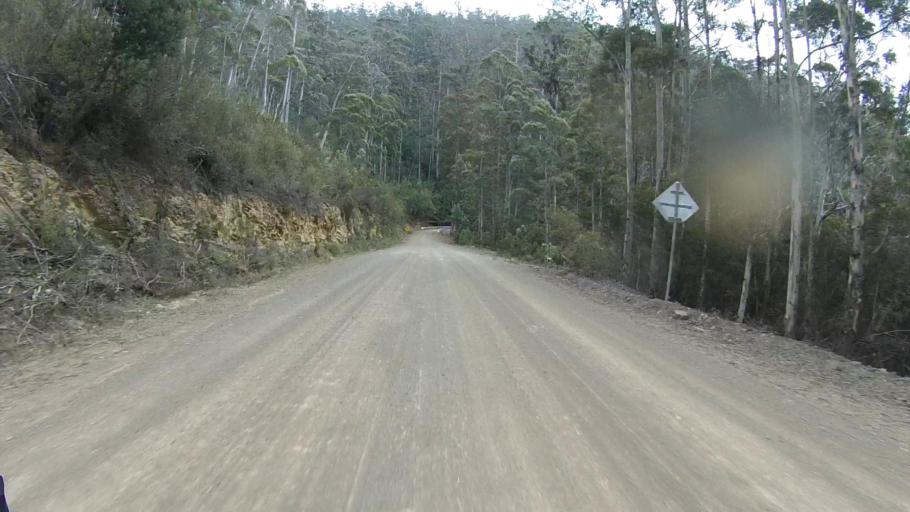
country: AU
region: Tasmania
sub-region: Sorell
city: Sorell
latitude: -42.6968
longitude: 147.8576
